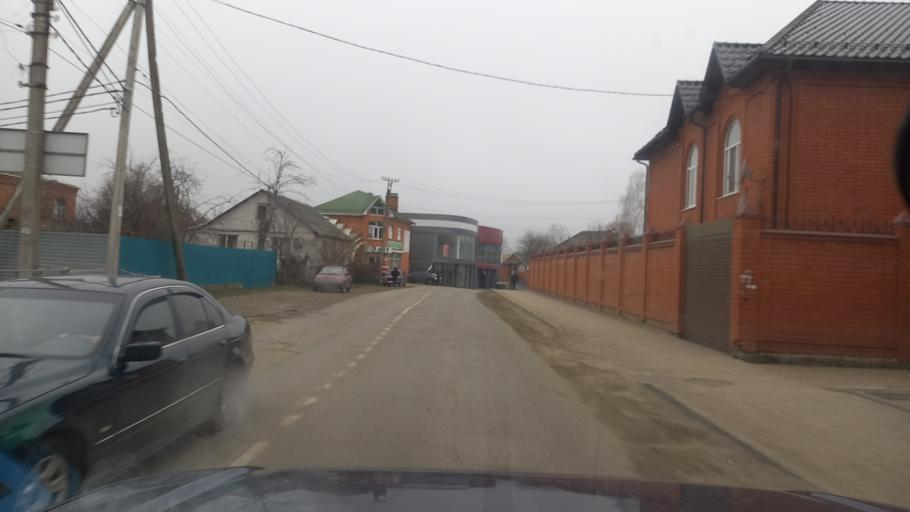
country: RU
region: Krasnodarskiy
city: Apsheronsk
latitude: 44.4625
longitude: 39.7409
